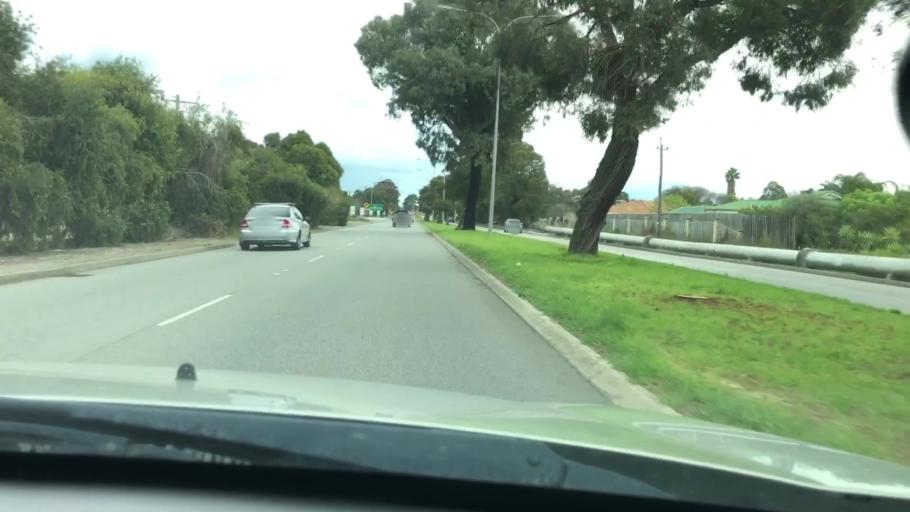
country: AU
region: Western Australia
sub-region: Armadale
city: Seville Grove
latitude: -32.1472
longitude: 115.9804
